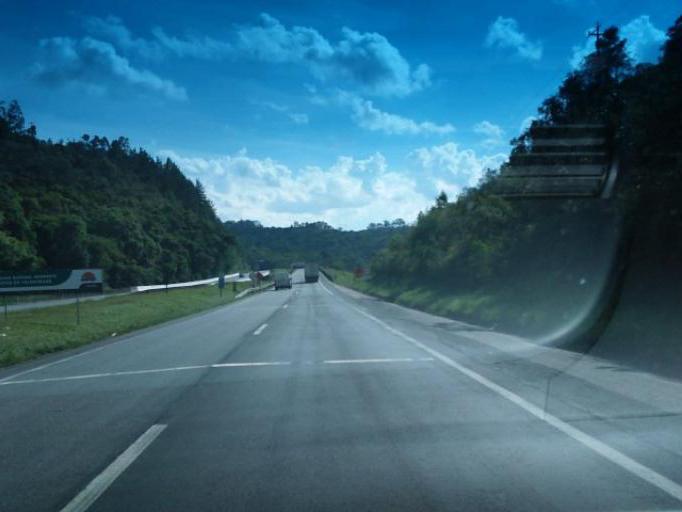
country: BR
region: Parana
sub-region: Campina Grande Do Sul
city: Campina Grande do Sul
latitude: -25.1664
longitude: -48.8643
